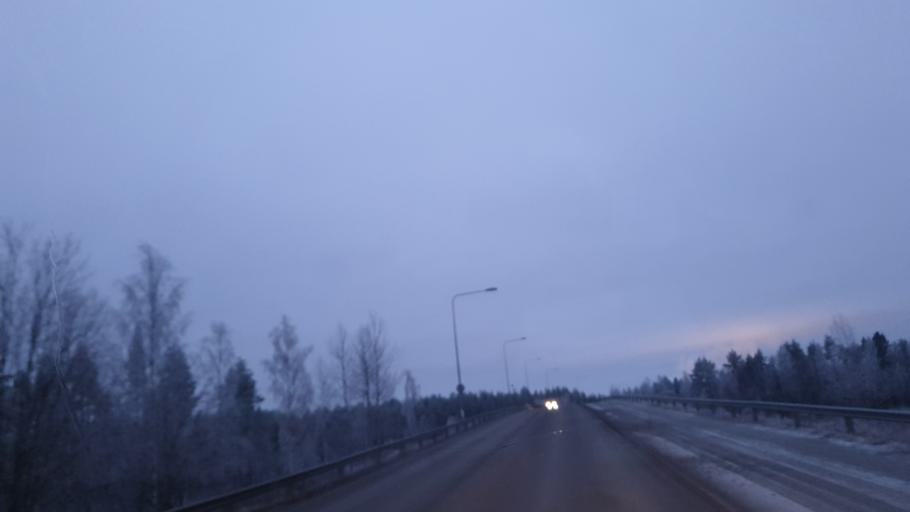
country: FI
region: Southern Ostrobothnia
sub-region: Seinaejoki
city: Nurmo
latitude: 62.7753
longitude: 22.8901
